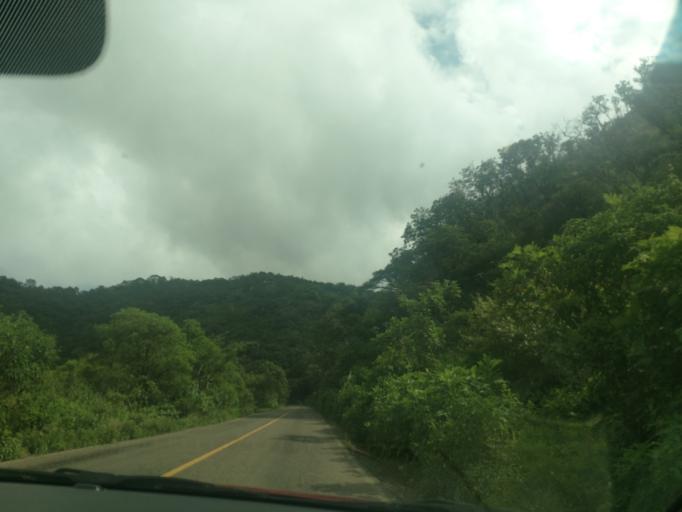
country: MX
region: Jalisco
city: El Salto
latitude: 20.3643
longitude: -104.5895
